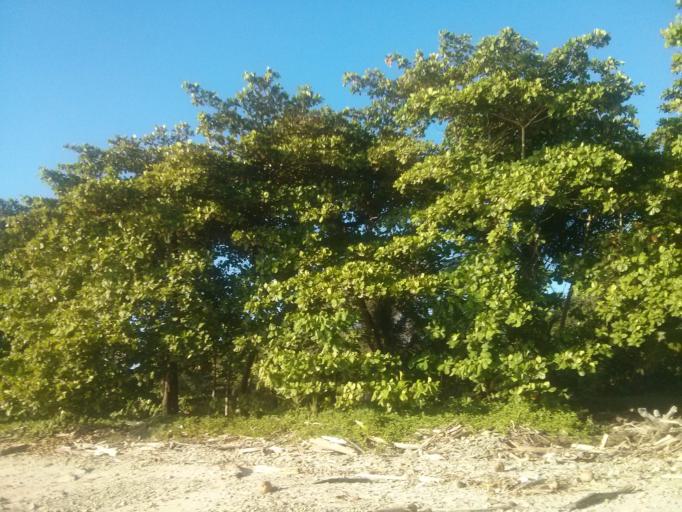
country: CR
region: Puntarenas
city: Paquera
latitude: 9.6176
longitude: -85.1460
